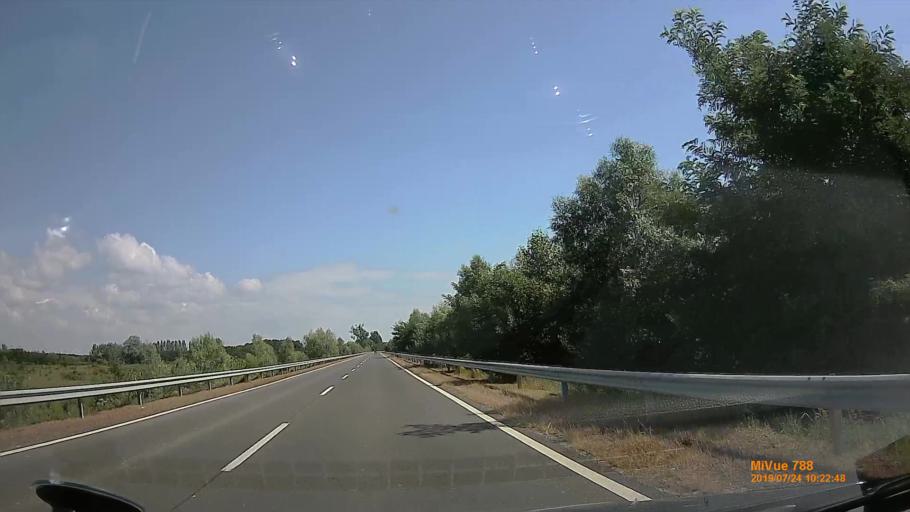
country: HU
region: Szabolcs-Szatmar-Bereg
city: Vasarosnameny
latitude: 48.1412
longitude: 22.3596
